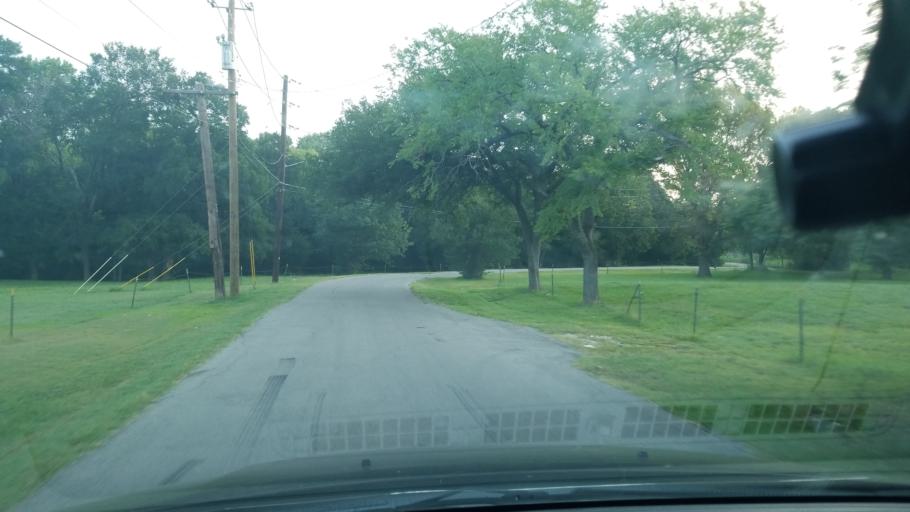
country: US
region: Texas
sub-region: Dallas County
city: Balch Springs
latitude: 32.7323
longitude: -96.6596
